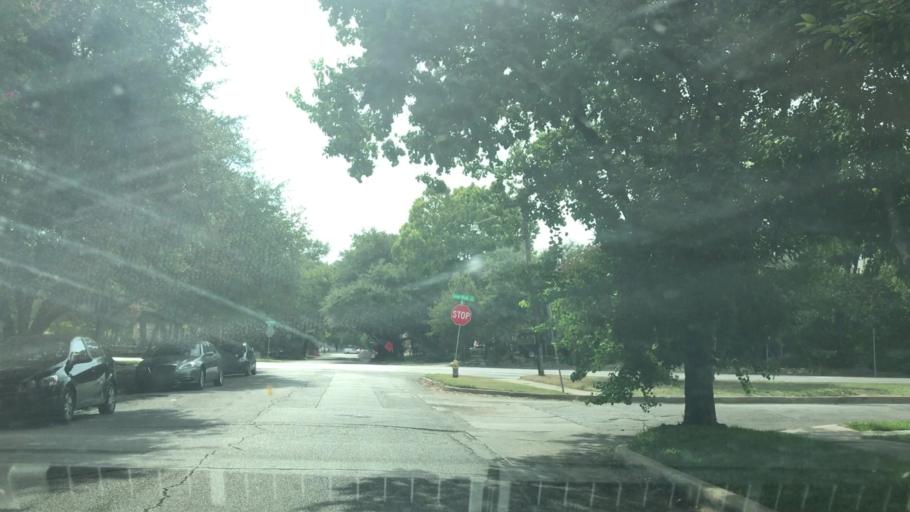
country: US
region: Texas
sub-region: Dallas County
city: Highland Park
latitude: 32.8070
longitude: -96.7666
